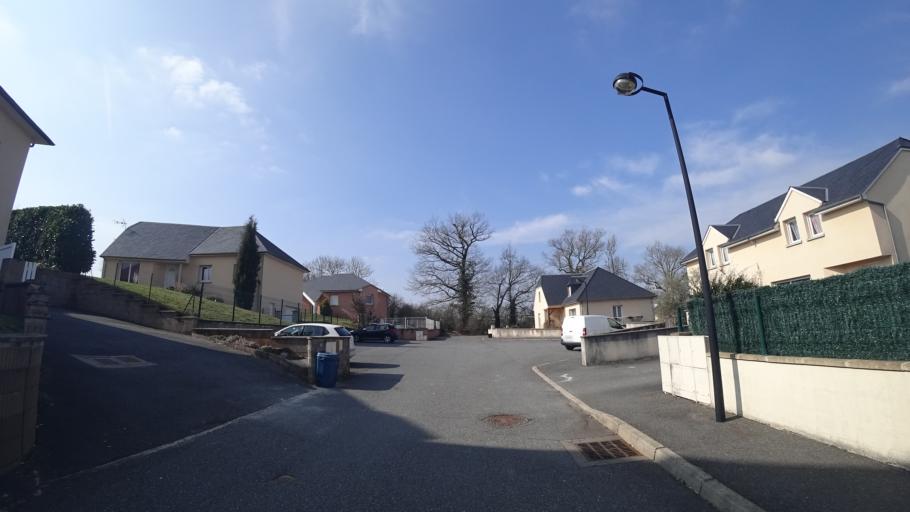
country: FR
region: Midi-Pyrenees
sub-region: Departement de l'Aveyron
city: Olemps
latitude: 44.3648
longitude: 2.5562
